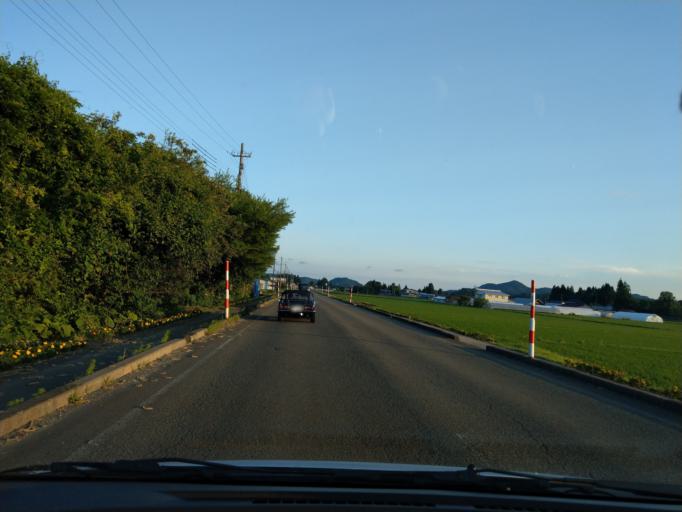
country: JP
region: Akita
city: Kakunodatemachi
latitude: 39.6501
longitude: 140.5707
